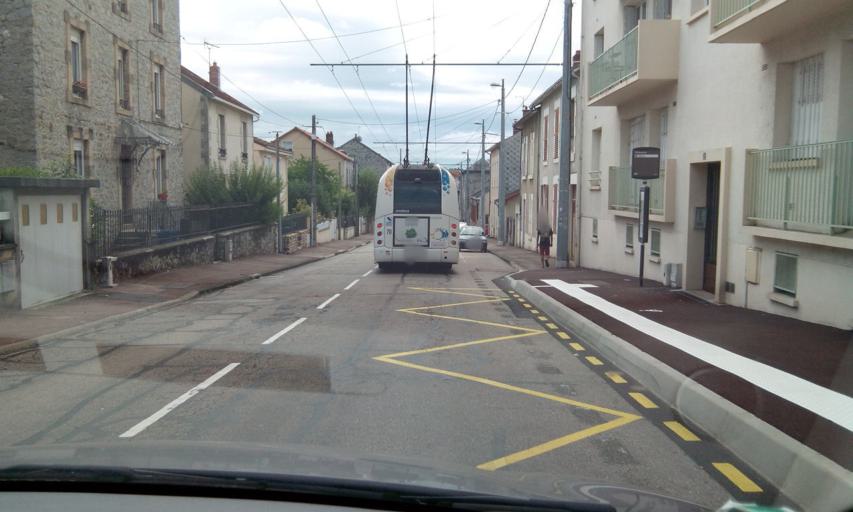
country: FR
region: Limousin
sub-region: Departement de la Haute-Vienne
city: Limoges
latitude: 45.8442
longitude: 1.2710
